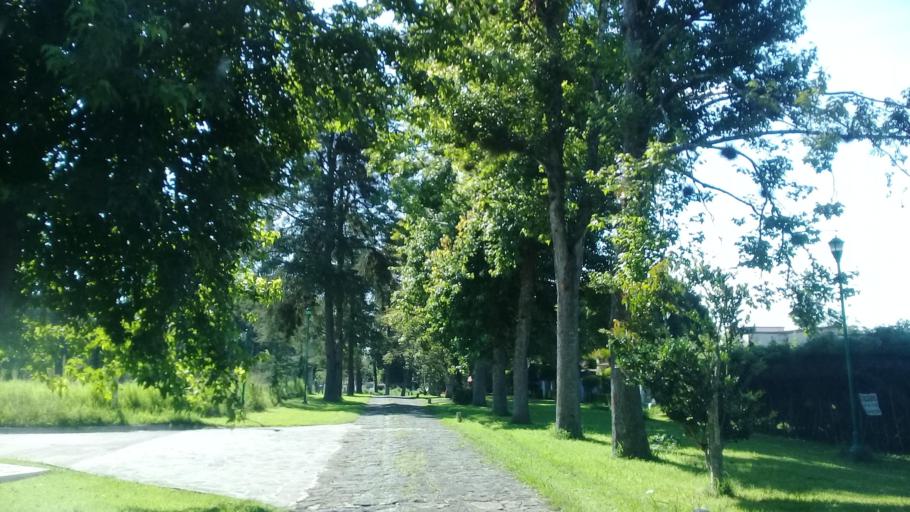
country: MX
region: Veracruz
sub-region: Tlalnelhuayocan
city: Guadalupe Victoria
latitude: 19.5340
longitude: -96.9489
